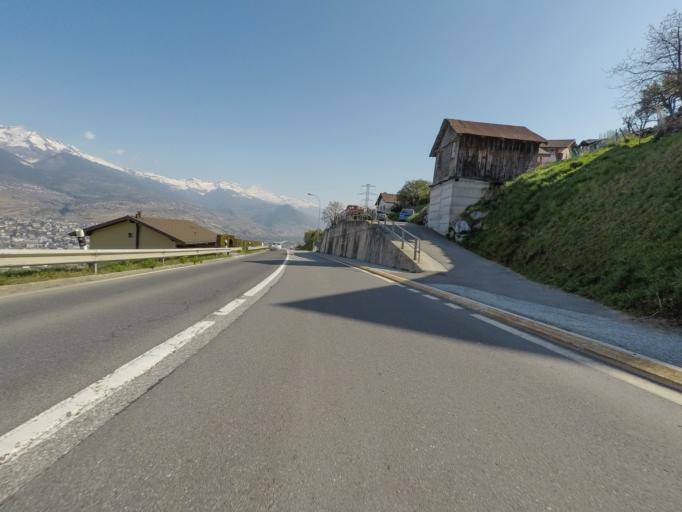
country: CH
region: Valais
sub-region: Sion District
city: Sitten
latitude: 46.2132
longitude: 7.3510
